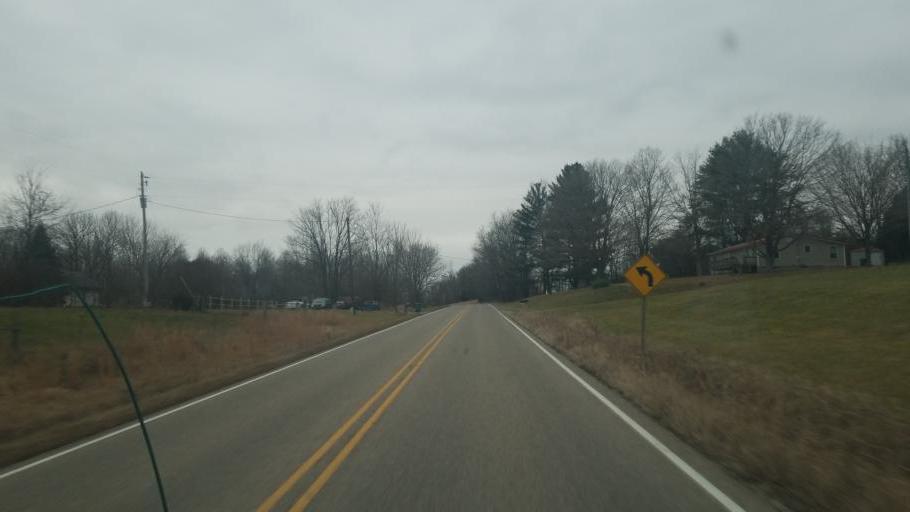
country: US
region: Indiana
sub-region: Owen County
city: Spencer
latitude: 39.3551
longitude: -86.9353
